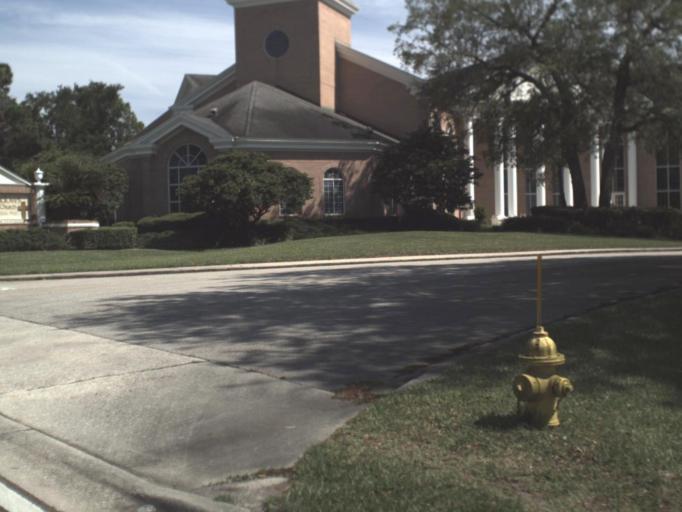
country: US
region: Florida
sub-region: Saint Johns County
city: Fruit Cove
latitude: 30.2196
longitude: -81.5569
